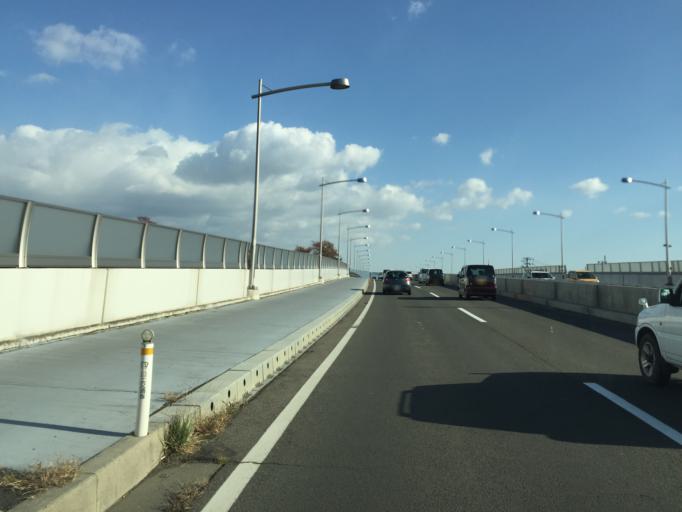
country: JP
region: Fukushima
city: Fukushima-shi
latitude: 37.7810
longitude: 140.4528
